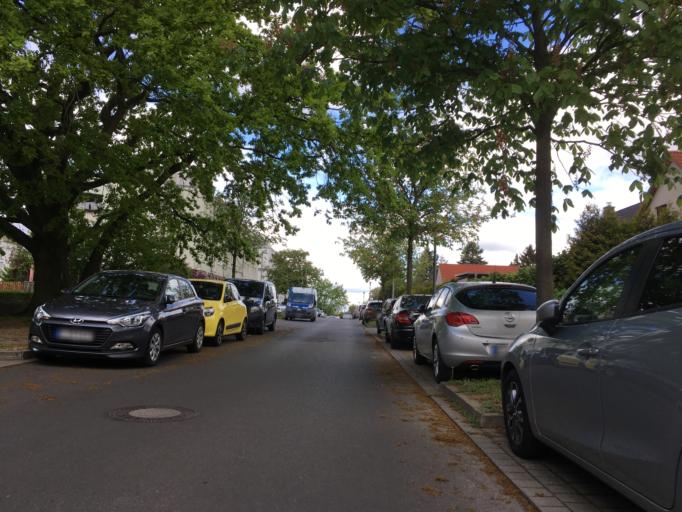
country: DE
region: Berlin
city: Buchholz
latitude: 52.6135
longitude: 13.4262
